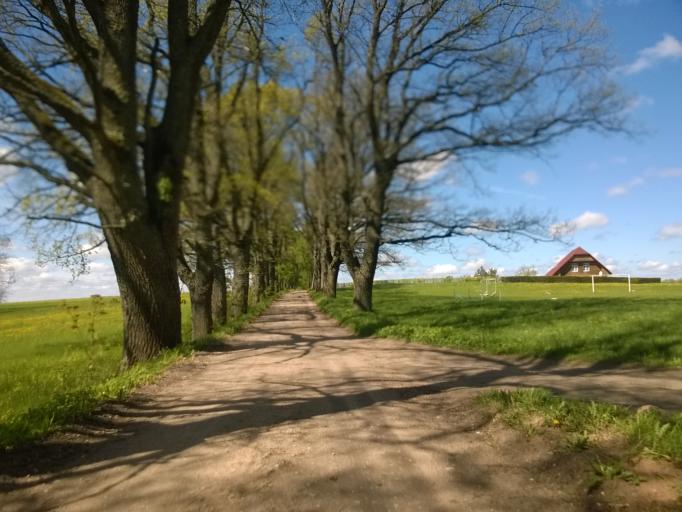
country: LV
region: Amatas Novads
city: Drabesi
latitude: 57.2453
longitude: 25.2771
